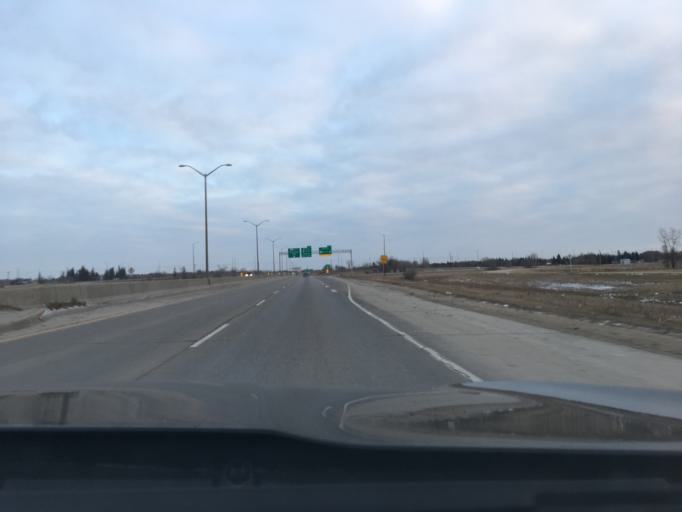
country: CA
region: Manitoba
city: Winnipeg
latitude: 49.9751
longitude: -97.0807
